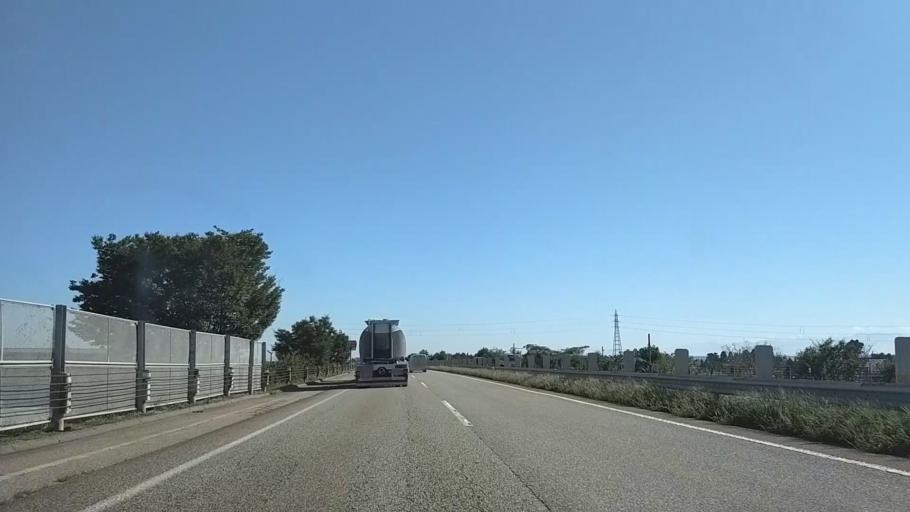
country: JP
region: Toyama
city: Nanto-shi
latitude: 36.6272
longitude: 136.9605
